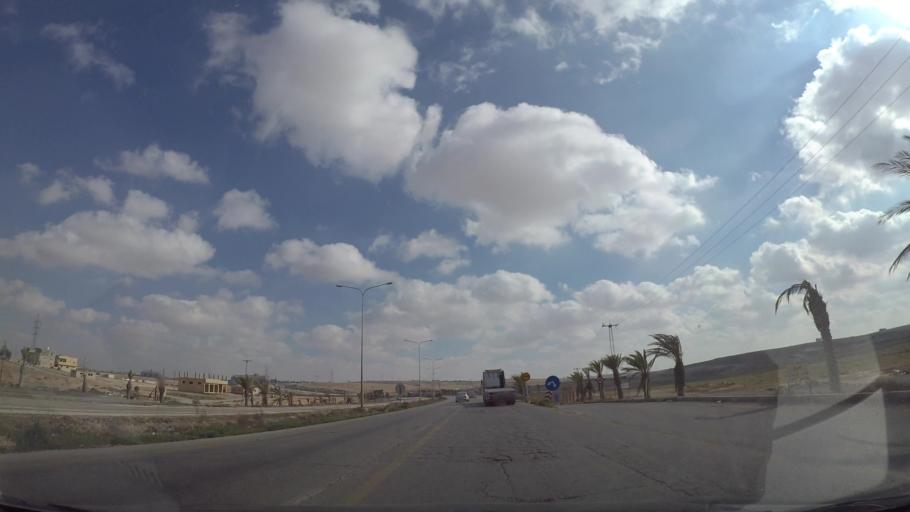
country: JO
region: Amman
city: Al Jizah
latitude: 31.6334
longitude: 35.9846
